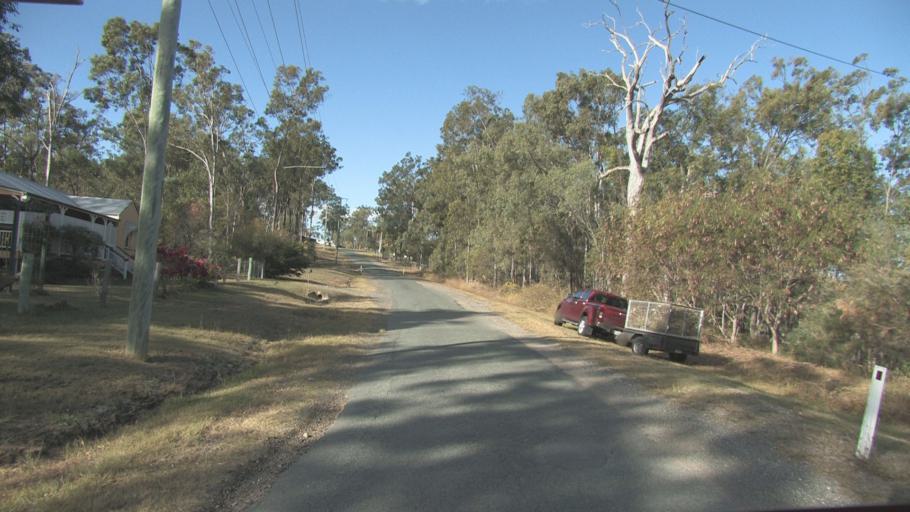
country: AU
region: Queensland
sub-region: Logan
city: Cedar Vale
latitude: -27.8472
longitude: 153.0653
